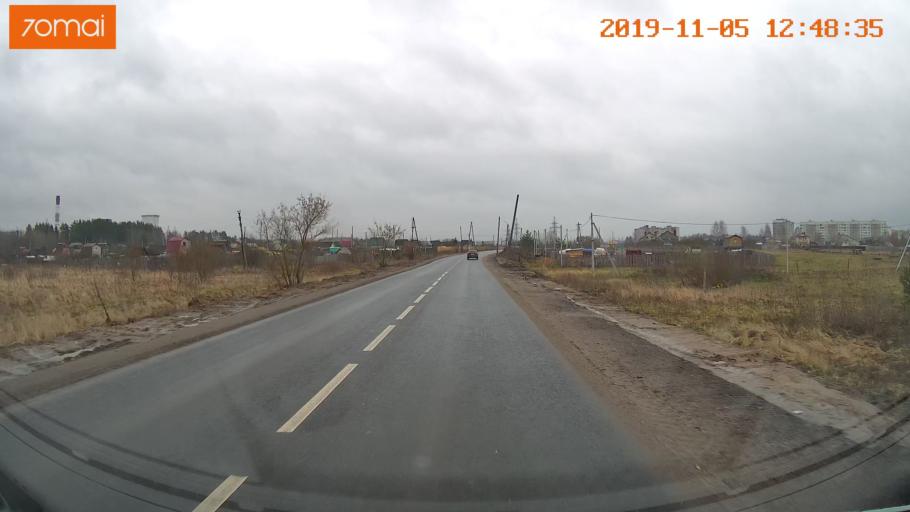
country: RU
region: Ivanovo
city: Kokhma
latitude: 56.9600
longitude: 41.0986
